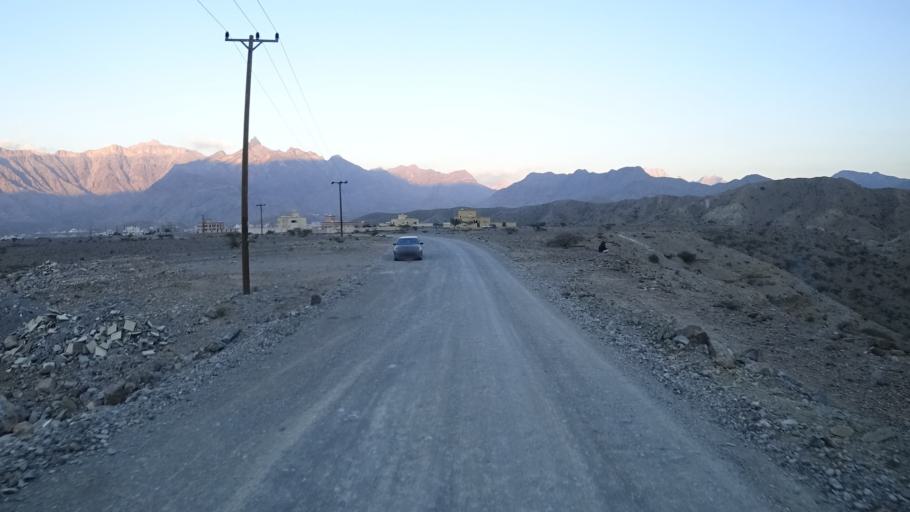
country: OM
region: Al Batinah
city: Rustaq
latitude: 23.2631
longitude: 57.3190
